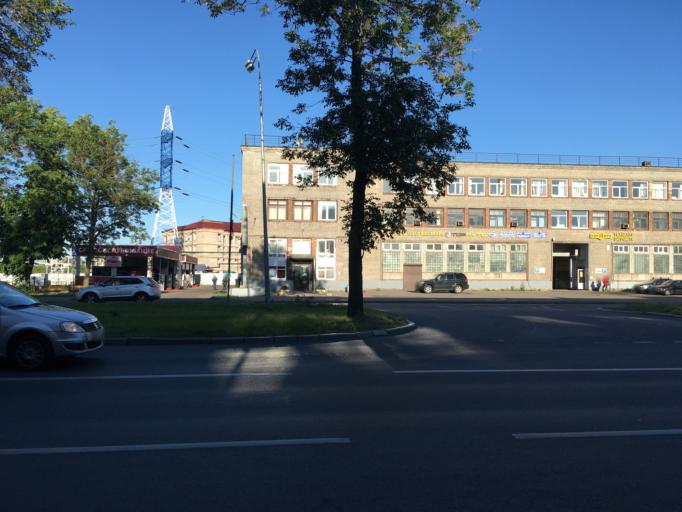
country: RU
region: St.-Petersburg
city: Centralniy
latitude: 59.8993
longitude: 30.3381
